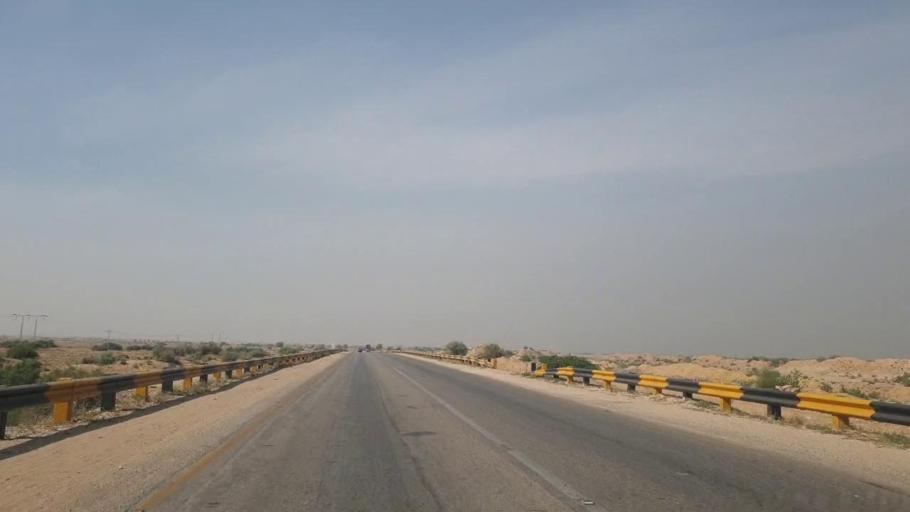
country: PK
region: Sindh
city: Sann
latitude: 26.0377
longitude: 68.1157
